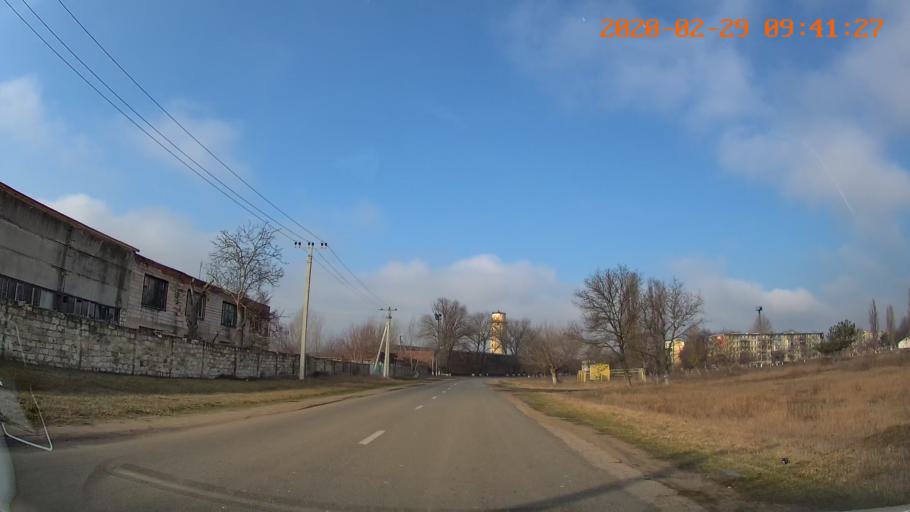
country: MD
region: Telenesti
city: Crasnoe
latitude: 46.6366
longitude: 29.8315
